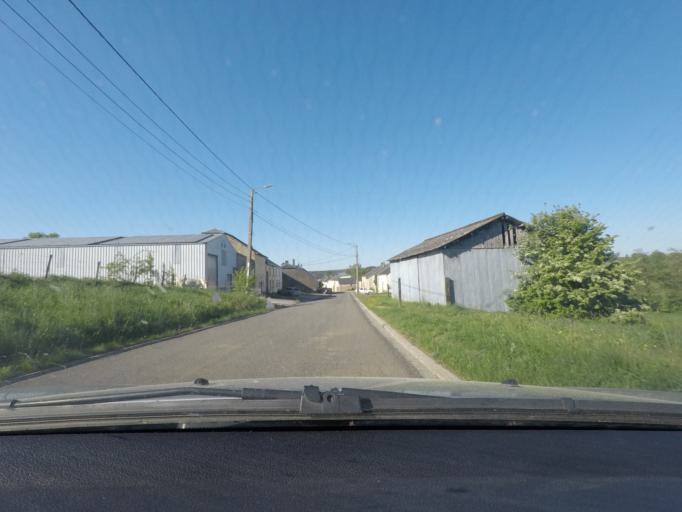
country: BE
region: Wallonia
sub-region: Province du Luxembourg
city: Tintigny
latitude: 49.7043
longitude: 5.4563
